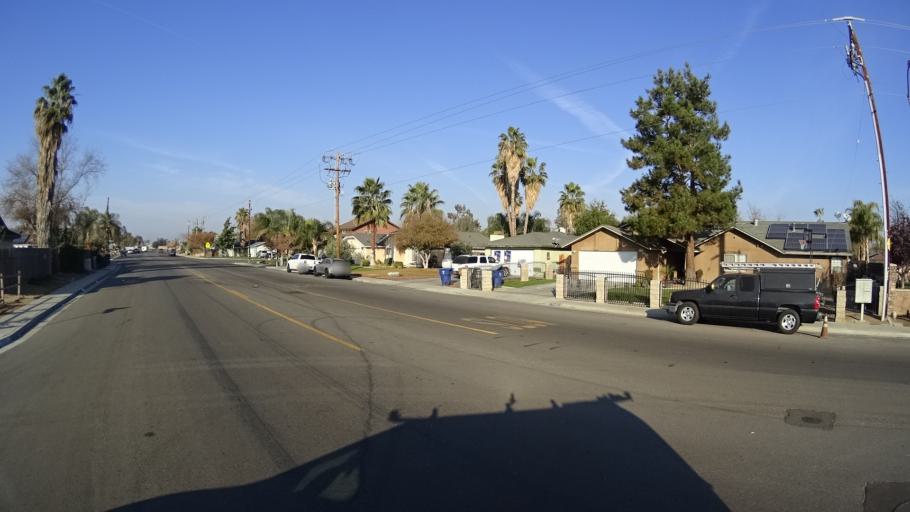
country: US
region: California
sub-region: Kern County
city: Greenfield
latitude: 35.3031
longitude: -119.0265
